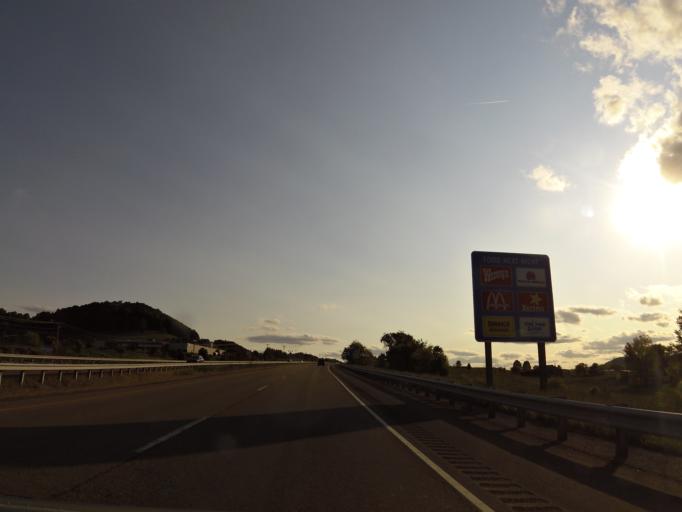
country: US
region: Virginia
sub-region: Russell County
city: Lebanon
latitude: 36.9026
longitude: -82.0476
